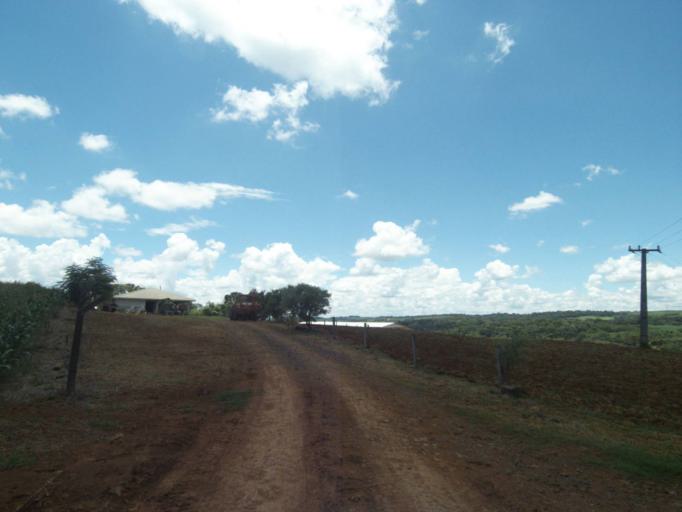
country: BR
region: Parana
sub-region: Pinhao
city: Pinhao
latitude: -25.7880
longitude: -52.0754
